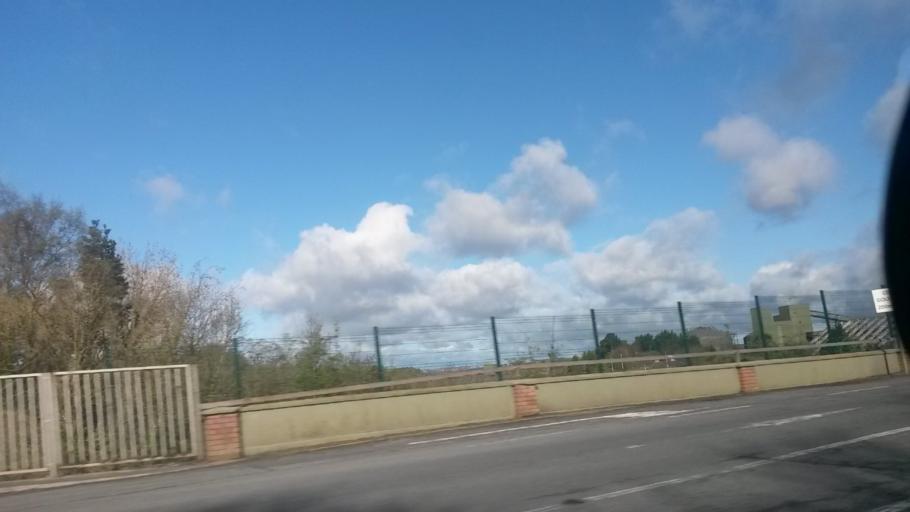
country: IE
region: Munster
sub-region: County Cork
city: Passage West
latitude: 51.8742
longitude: -8.3239
